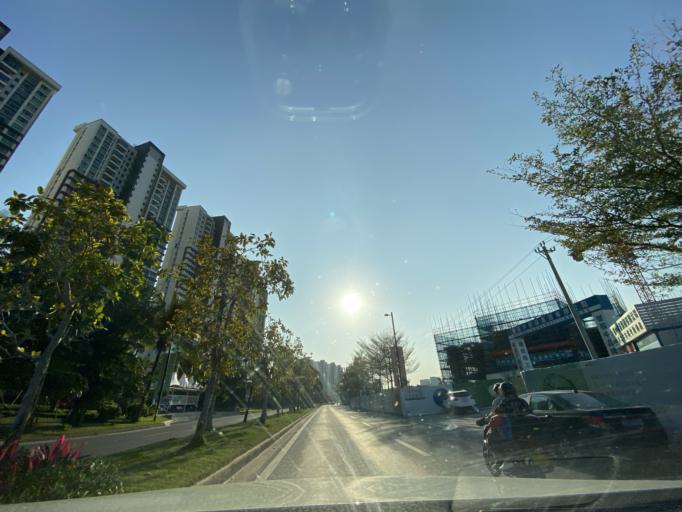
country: CN
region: Hainan
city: Xincun
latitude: 18.4230
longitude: 109.9256
